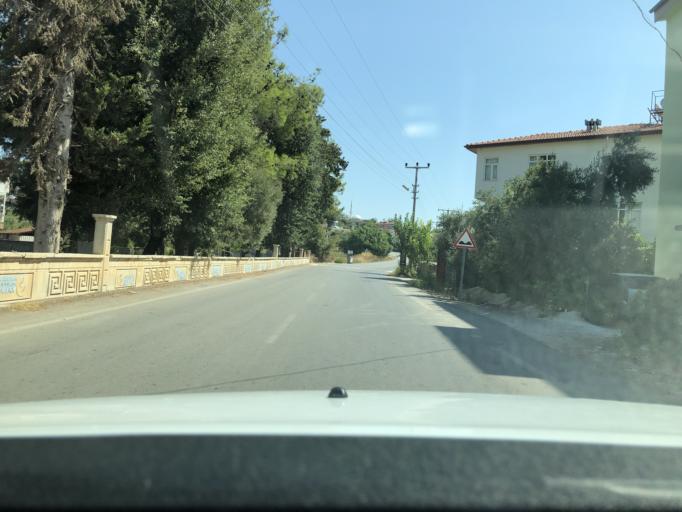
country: TR
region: Antalya
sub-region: Manavgat
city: Manavgat
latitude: 36.8104
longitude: 31.4837
